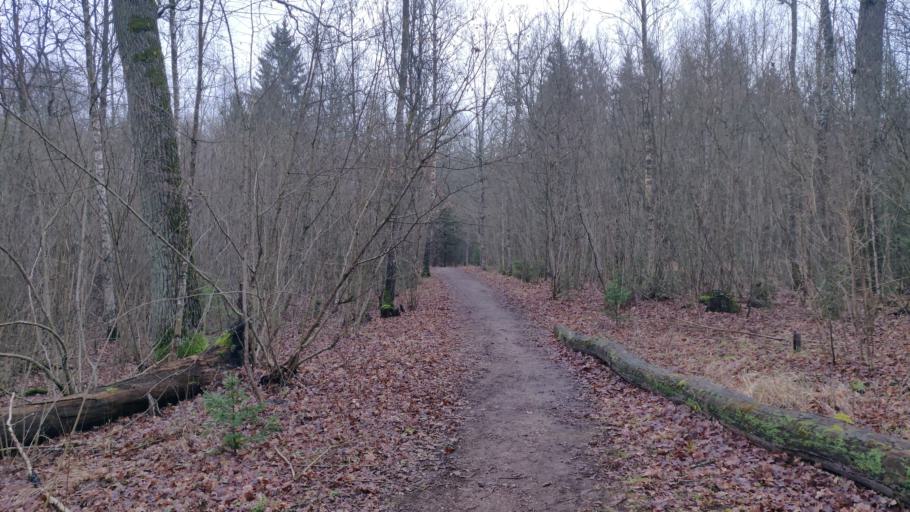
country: LT
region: Vilnius County
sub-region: Vilniaus Rajonas
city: Vievis
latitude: 54.8362
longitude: 24.9534
